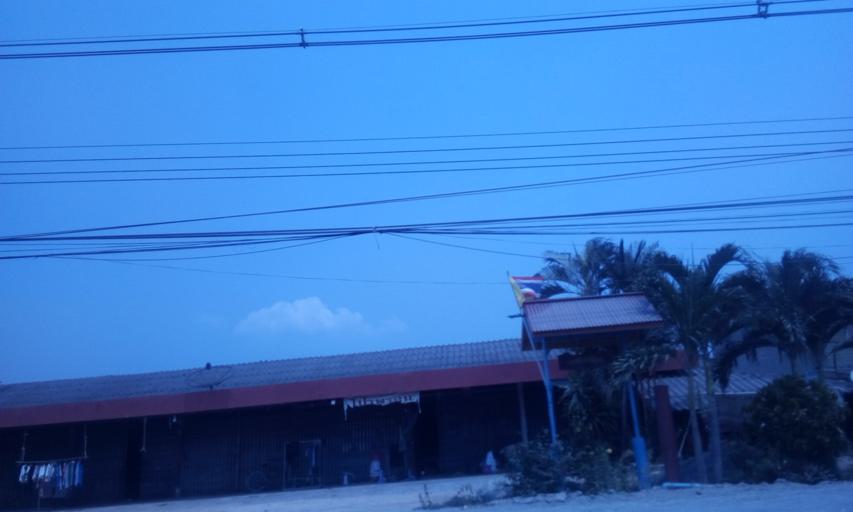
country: TH
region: Chachoengsao
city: Ban Pho
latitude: 13.5574
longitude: 101.1367
